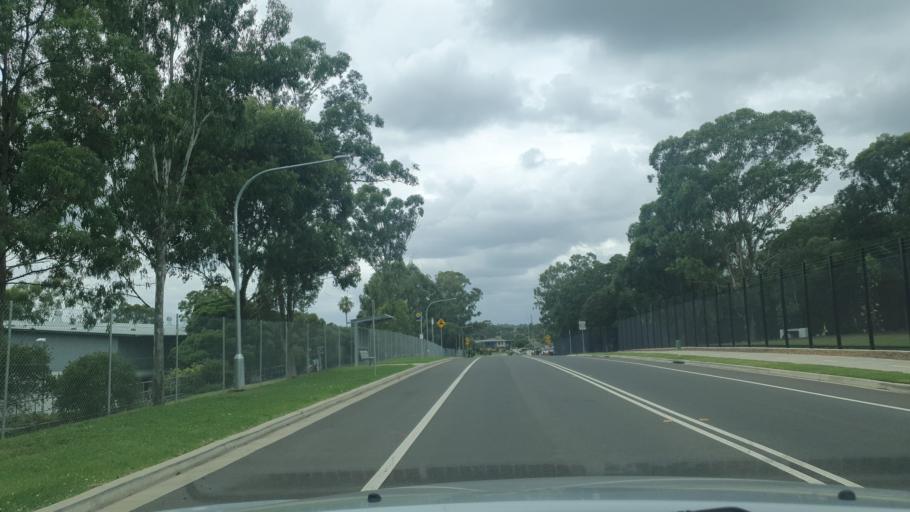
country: AU
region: New South Wales
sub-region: Penrith Municipality
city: Werrington County
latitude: -33.7716
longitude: 150.7421
